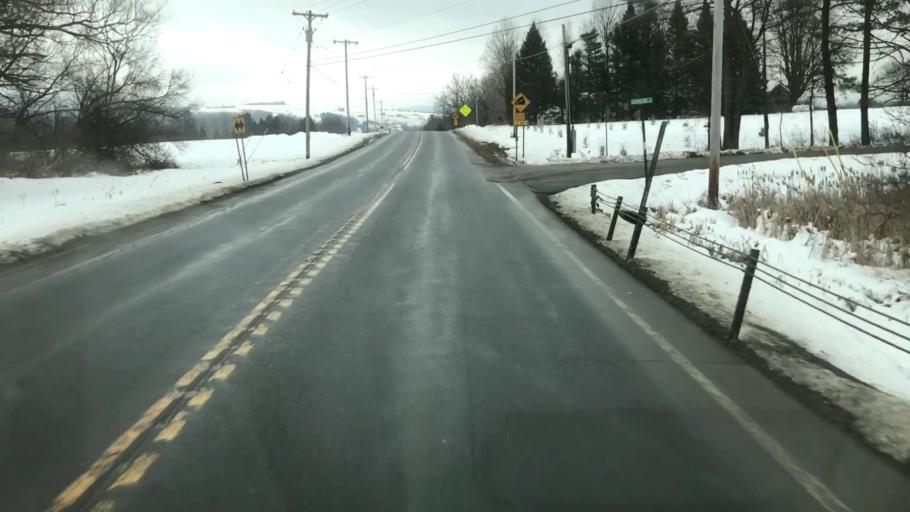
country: US
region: New York
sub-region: Cortland County
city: Homer
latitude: 42.6380
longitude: -76.2081
